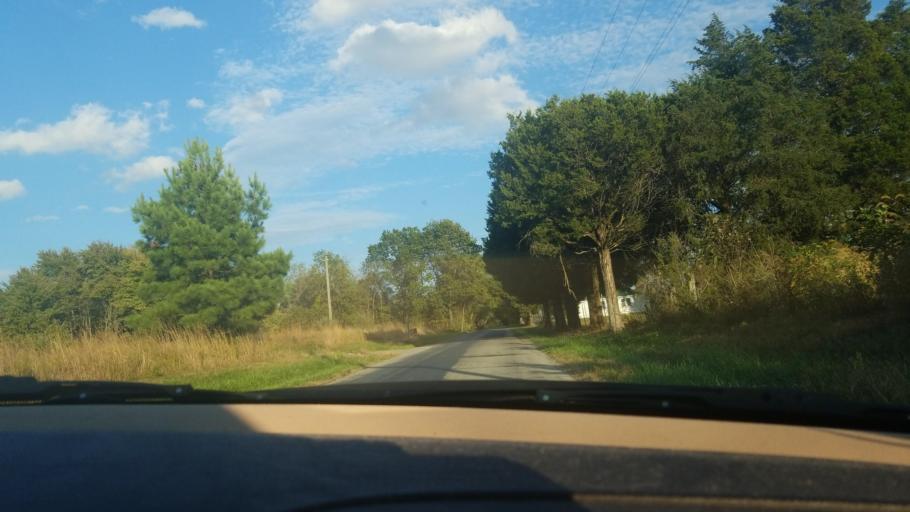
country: US
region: Illinois
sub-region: Saline County
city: Carrier Mills
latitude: 37.7720
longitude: -88.7223
